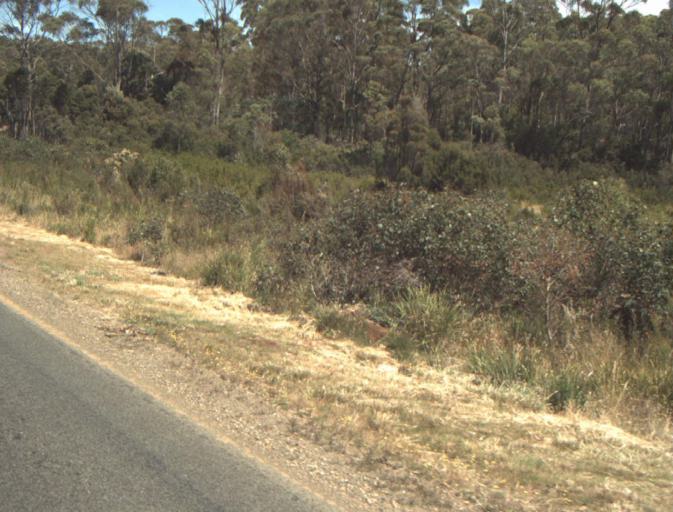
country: AU
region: Tasmania
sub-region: Launceston
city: Mayfield
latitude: -41.3037
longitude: 147.1335
